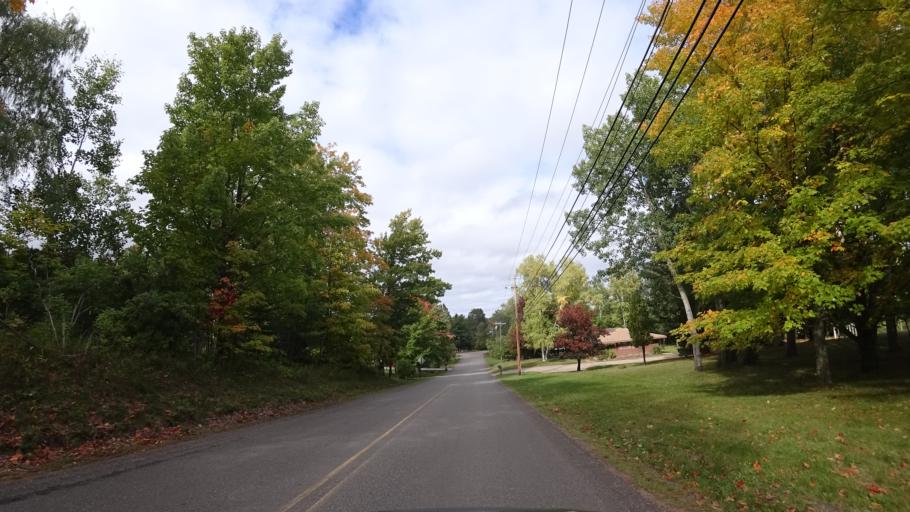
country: US
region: Michigan
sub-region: Marquette County
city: Trowbridge Park
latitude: 46.5462
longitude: -87.4374
